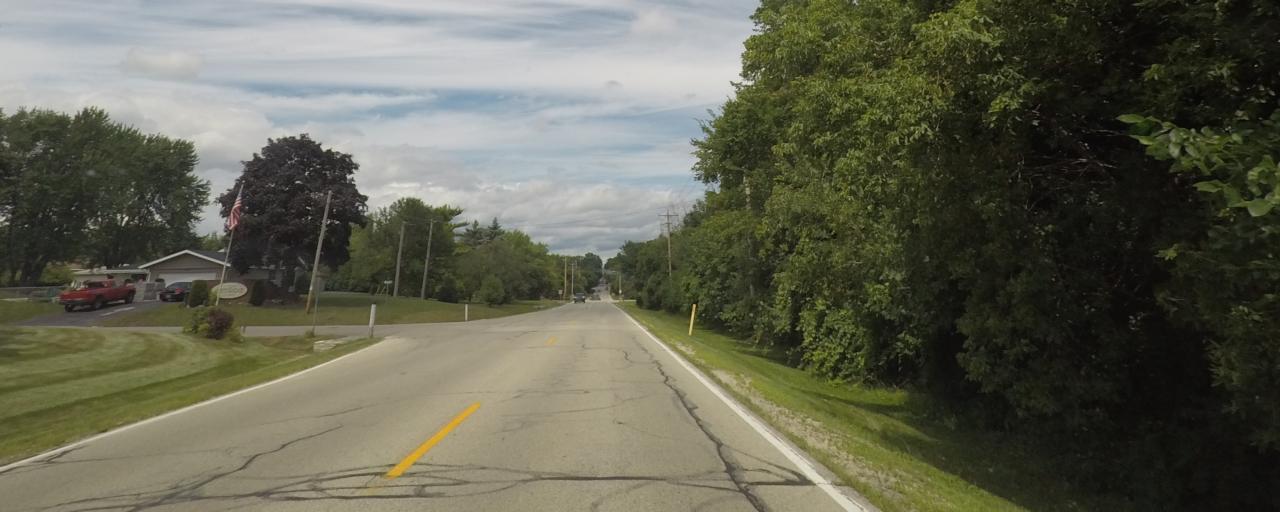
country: US
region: Wisconsin
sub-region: Waukesha County
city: New Berlin
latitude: 42.9795
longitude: -88.0687
